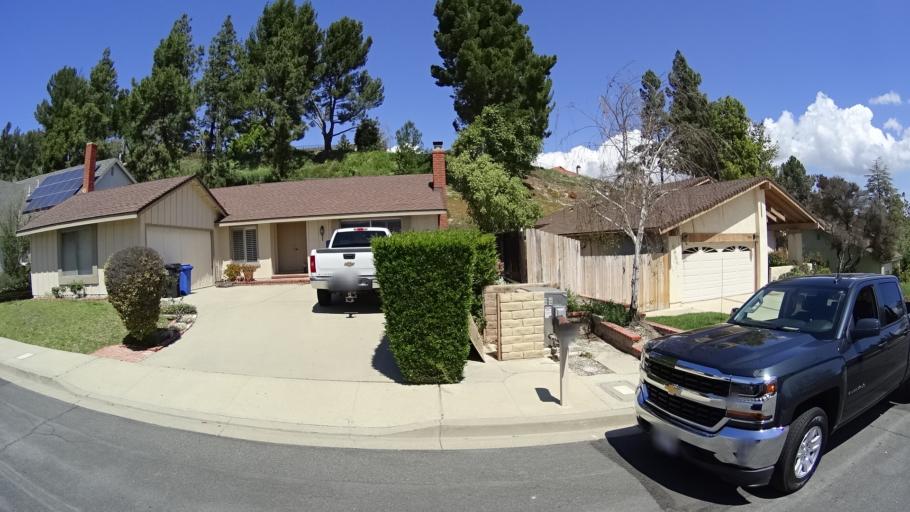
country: US
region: California
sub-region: Ventura County
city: Thousand Oaks
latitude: 34.2201
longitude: -118.8447
